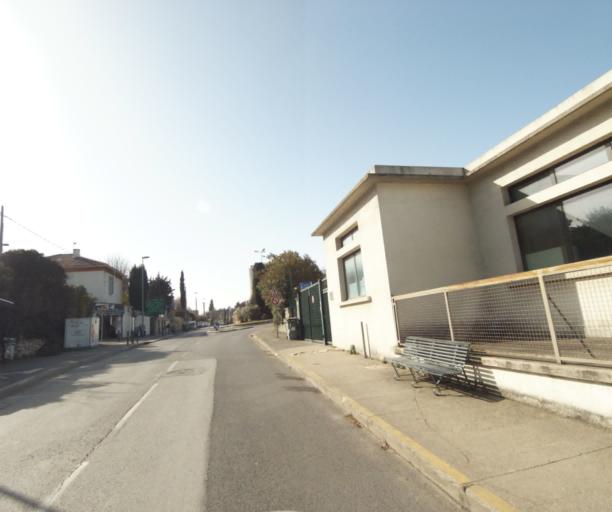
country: FR
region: Provence-Alpes-Cote d'Azur
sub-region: Departement des Bouches-du-Rhone
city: Aix-en-Provence
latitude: 43.5381
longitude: 5.4531
